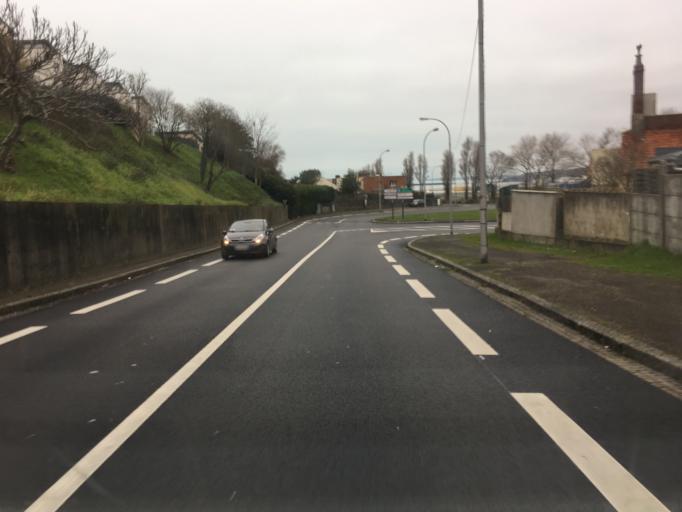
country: FR
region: Nord-Pas-de-Calais
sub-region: Departement du Pas-de-Calais
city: Outreau
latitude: 50.7176
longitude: 1.5907
